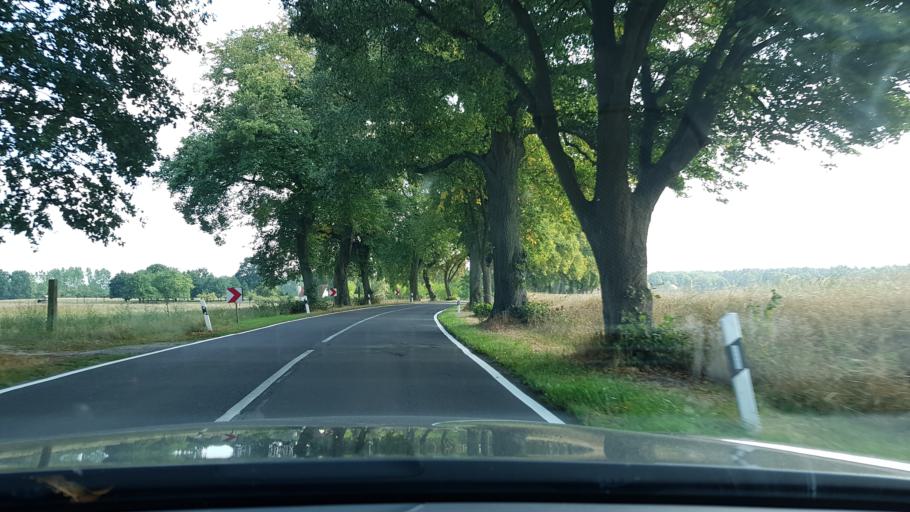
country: DE
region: Brandenburg
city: Lindow
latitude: 52.9875
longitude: 12.9765
